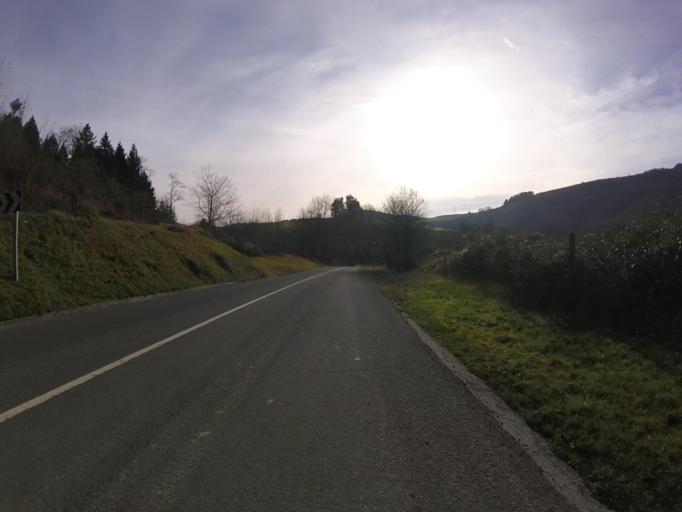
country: ES
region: Navarre
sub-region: Provincia de Navarra
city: Areso
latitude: 43.1017
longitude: -1.9531
